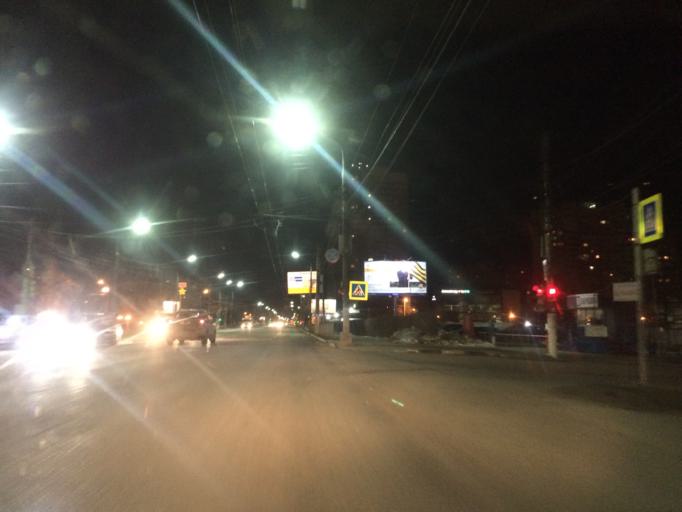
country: RU
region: Tula
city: Mendeleyevskiy
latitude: 54.1584
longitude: 37.5854
